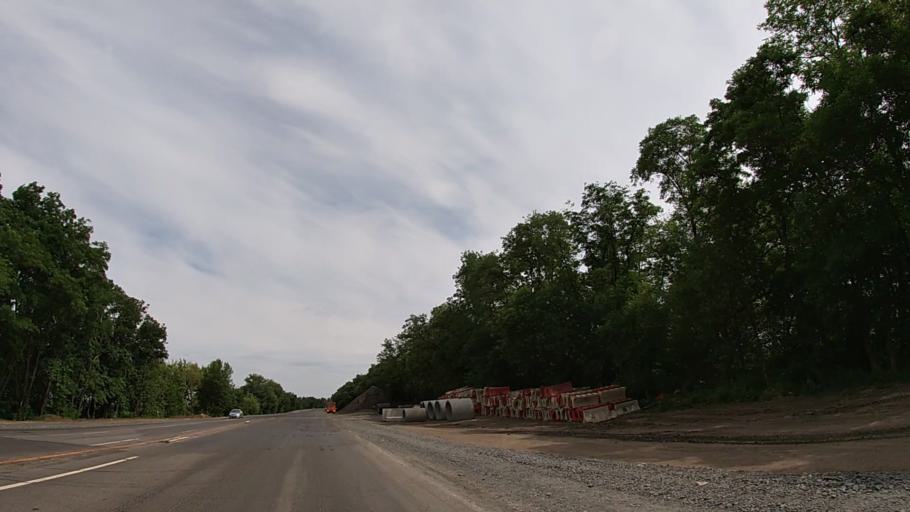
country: RU
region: Belgorod
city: Mayskiy
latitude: 50.4773
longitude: 36.4057
